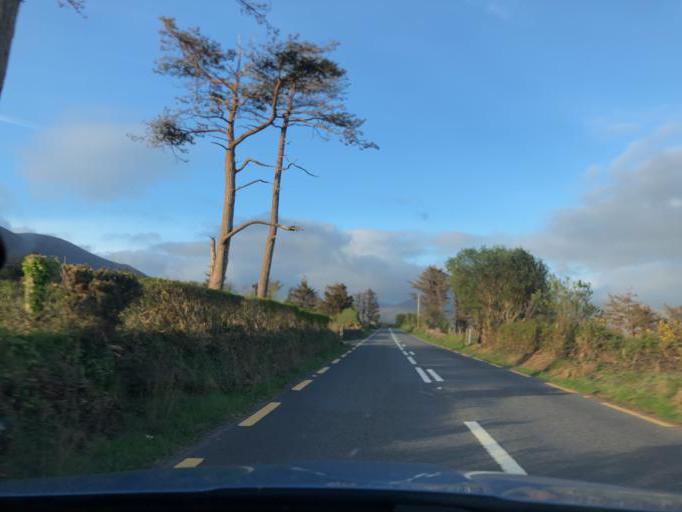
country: IE
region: Munster
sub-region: Ciarrai
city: Cahersiveen
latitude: 51.9752
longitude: -10.1621
